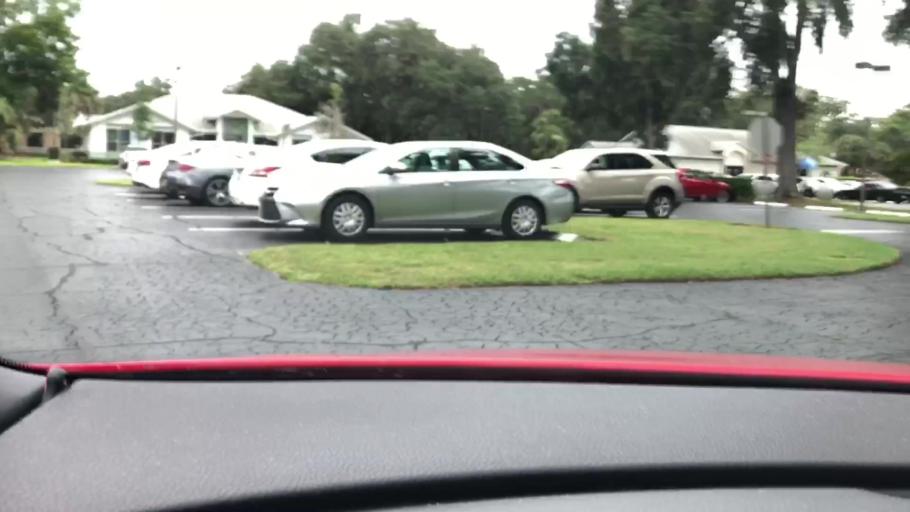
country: US
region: Florida
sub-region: Flagler County
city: Palm Coast
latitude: 29.5596
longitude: -81.2040
